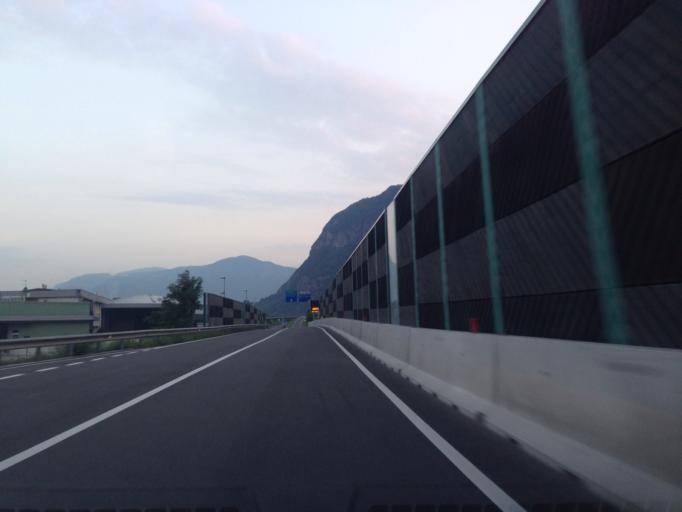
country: IT
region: Trentino-Alto Adige
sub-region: Bolzano
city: Pineta
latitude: 46.4384
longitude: 11.3443
